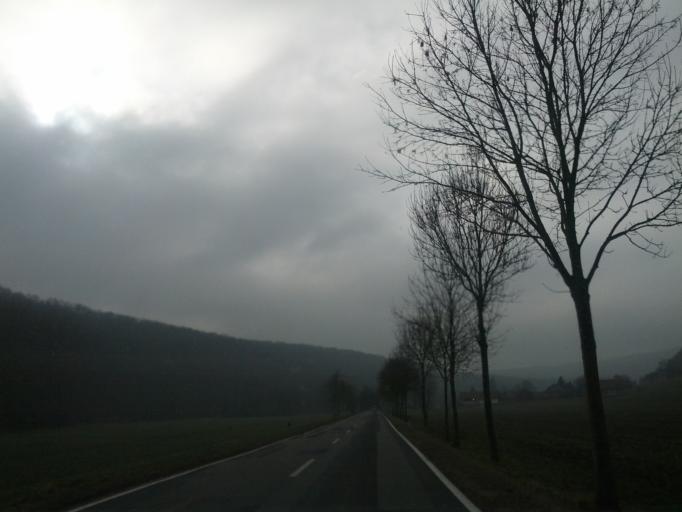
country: DE
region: Thuringia
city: Ebenshausen
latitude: 51.0756
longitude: 10.2992
